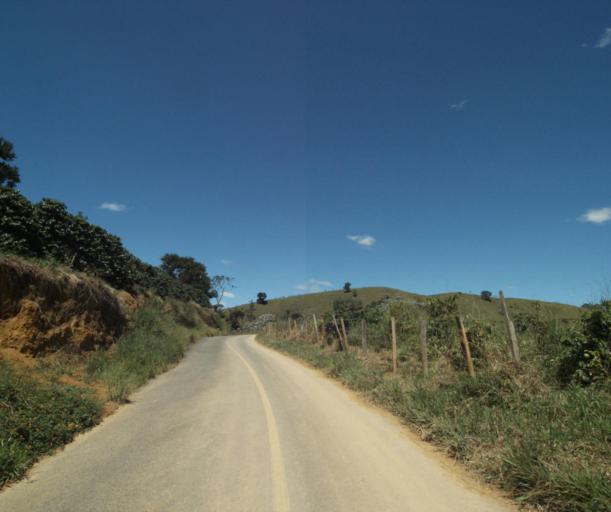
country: BR
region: Minas Gerais
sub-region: Espera Feliz
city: Espera Feliz
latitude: -20.6384
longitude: -41.8106
